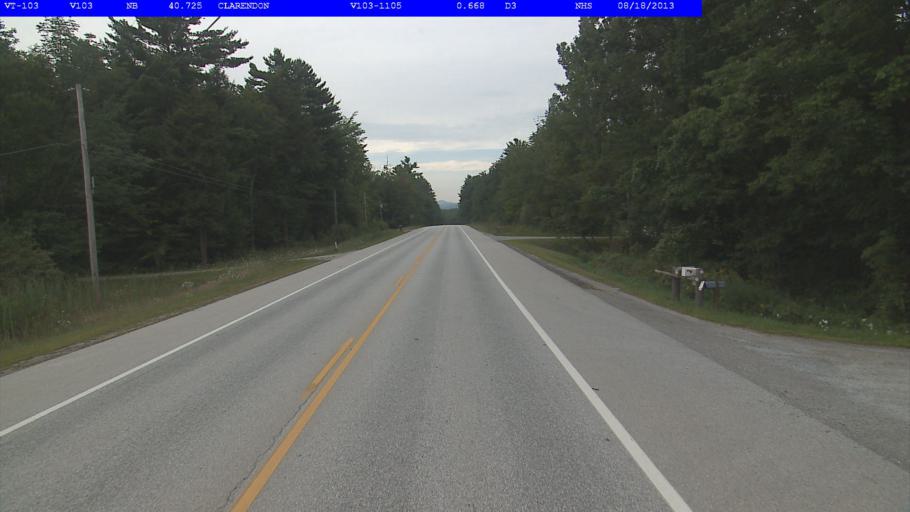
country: US
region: Vermont
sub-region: Rutland County
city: Rutland
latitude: 43.5319
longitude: -72.9381
